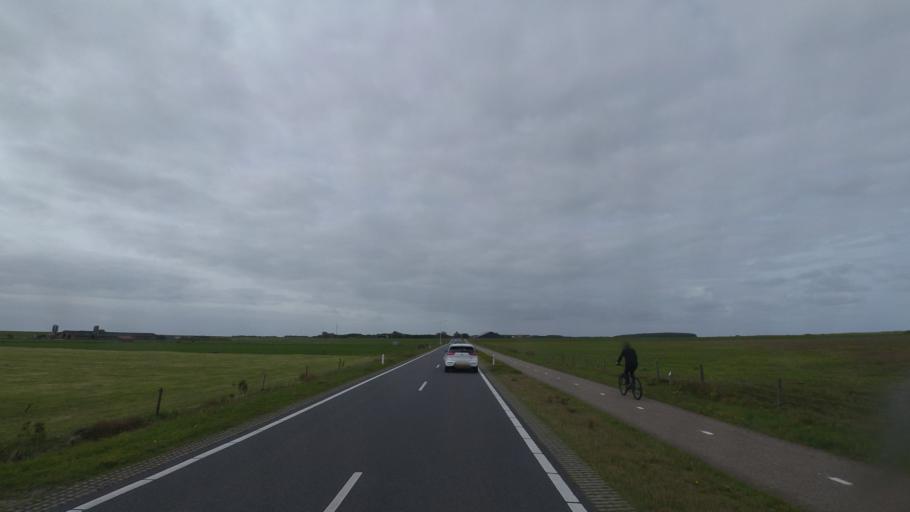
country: NL
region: Friesland
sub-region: Gemeente Ameland
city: Nes
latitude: 53.4461
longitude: 5.7379
